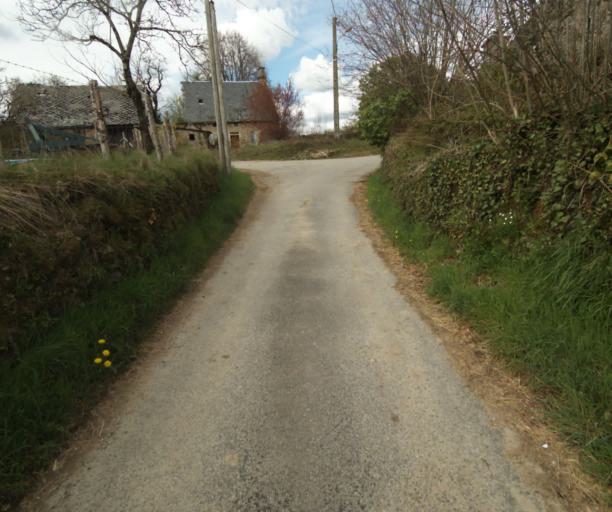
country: FR
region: Limousin
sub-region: Departement de la Correze
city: Argentat
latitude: 45.1811
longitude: 1.9222
